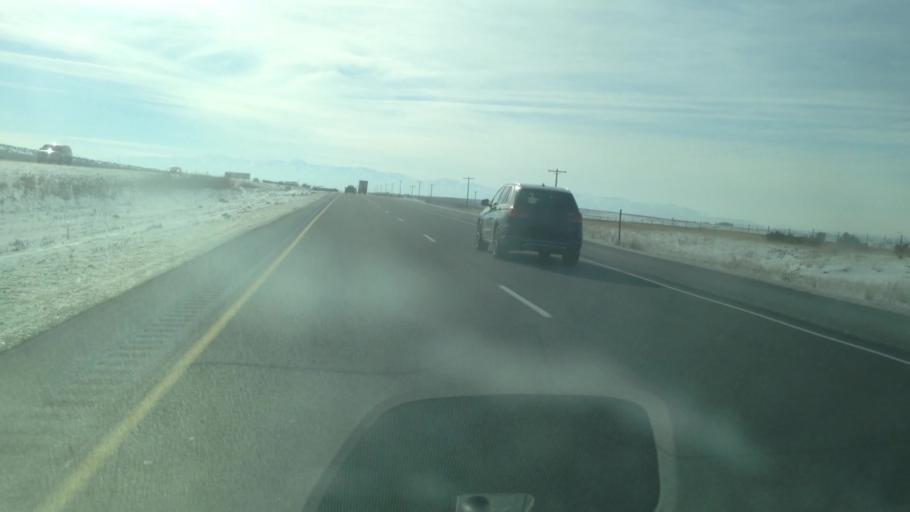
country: US
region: Idaho
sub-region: Bingham County
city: Fort Hall
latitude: 42.9945
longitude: -112.4145
